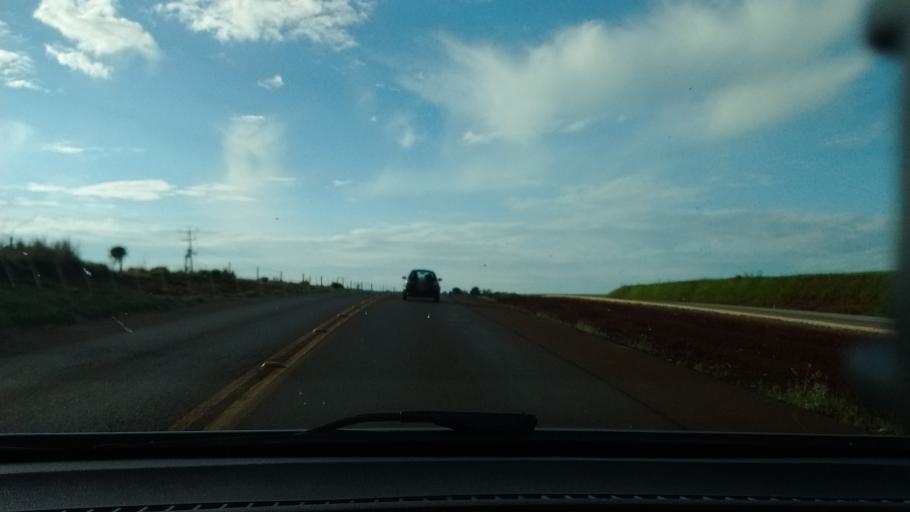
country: BR
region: Parana
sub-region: Cascavel
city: Cascavel
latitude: -25.1016
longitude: -53.5927
